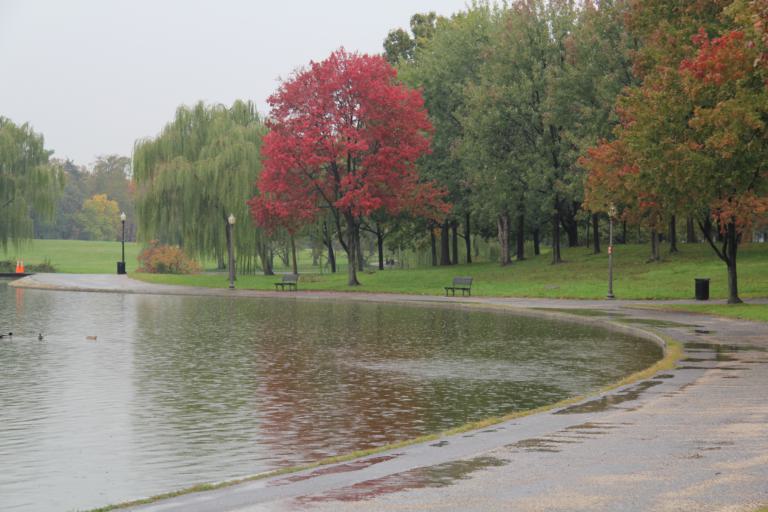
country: US
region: Washington, D.C.
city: Washington, D.C.
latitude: 38.8911
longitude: -77.0419
